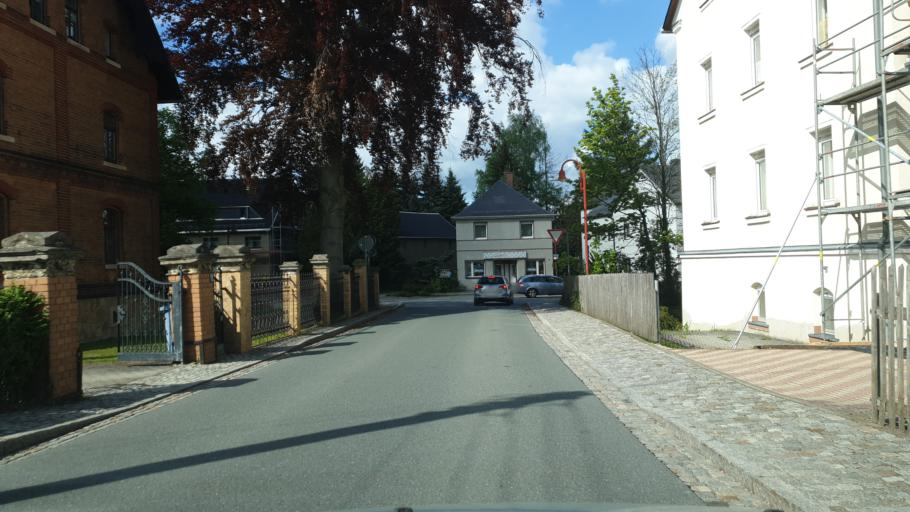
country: DE
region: Saxony
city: Lugau
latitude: 50.7204
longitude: 12.7481
